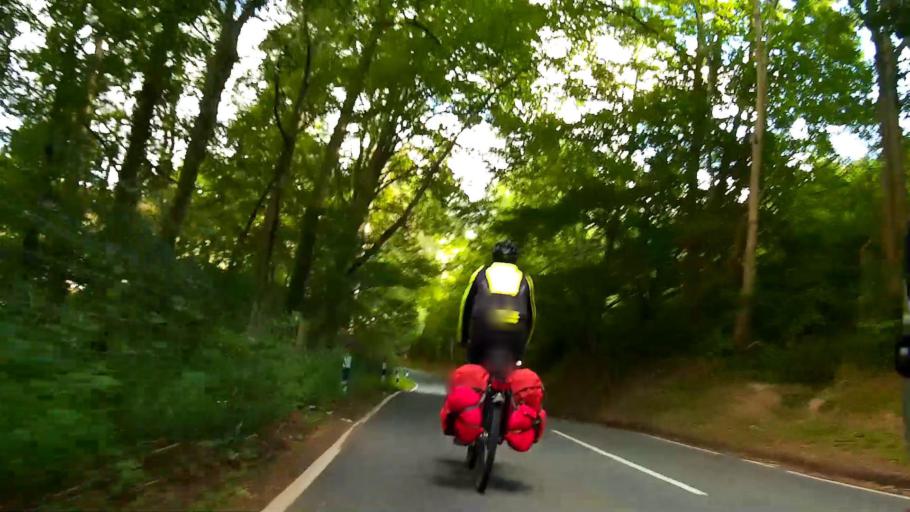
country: GB
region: Wales
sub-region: Denbighshire
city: Llangollen
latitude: 53.0052
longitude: -3.1919
